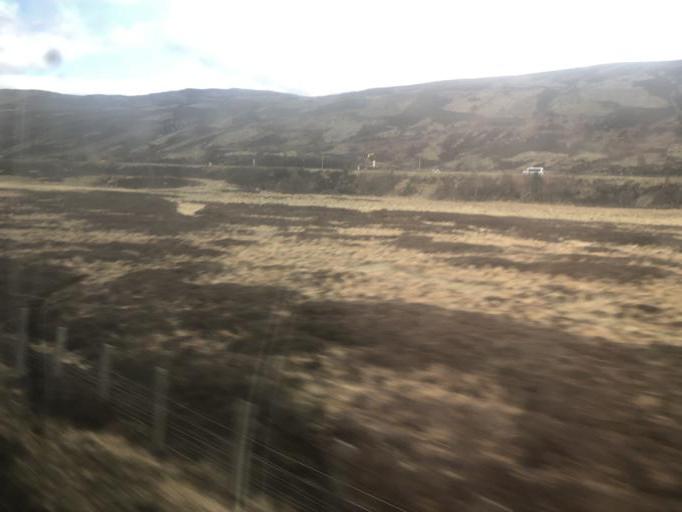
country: GB
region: Scotland
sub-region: Highland
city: Kingussie
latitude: 56.9757
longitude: -4.1861
